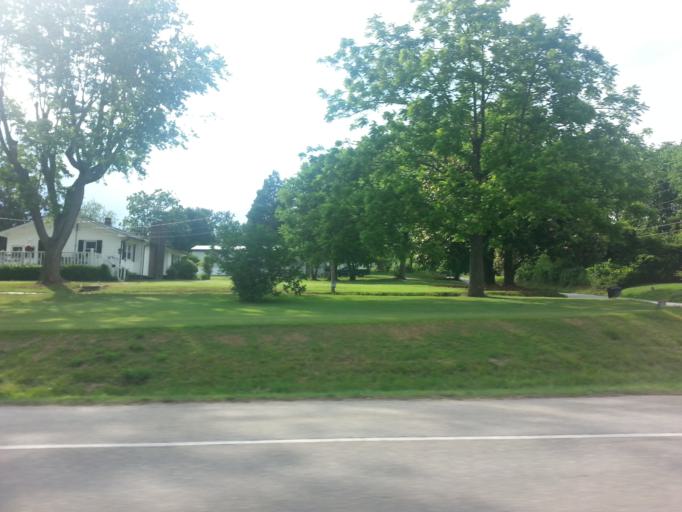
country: US
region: Tennessee
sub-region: Blount County
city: Louisville
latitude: 35.8220
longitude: -84.0232
